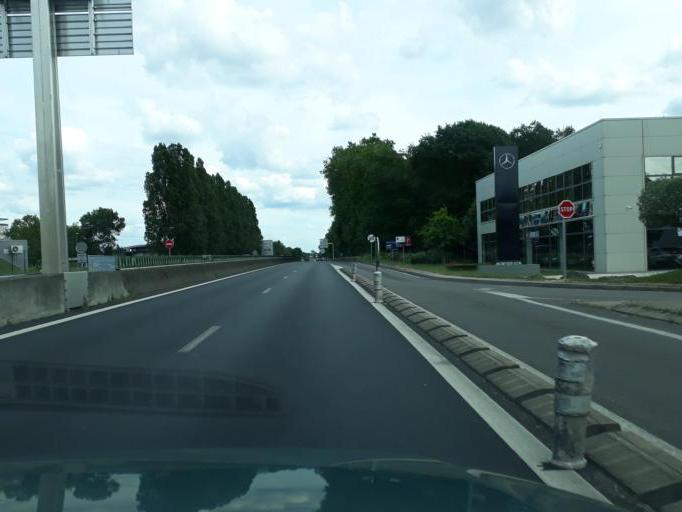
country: FR
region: Centre
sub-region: Departement du Loiret
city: Olivet
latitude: 47.8376
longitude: 1.9153
